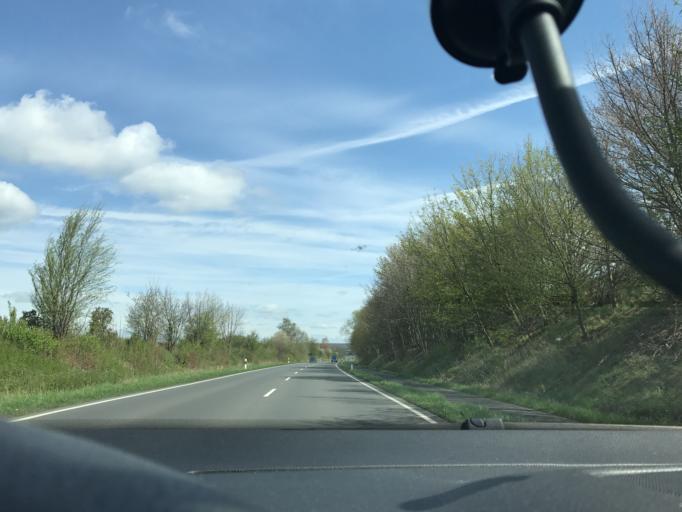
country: DE
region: Lower Saxony
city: Helmstedt
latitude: 52.2080
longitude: 10.9839
